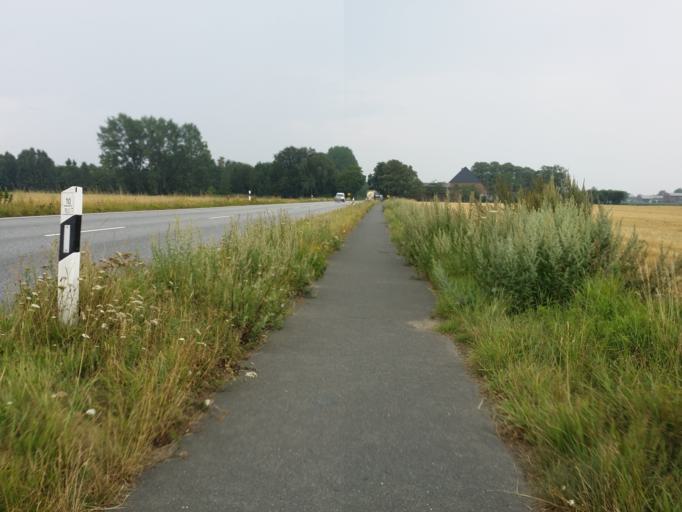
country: DE
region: Schleswig-Holstein
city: Blomesche Wildnis
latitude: 53.8094
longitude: 9.4227
